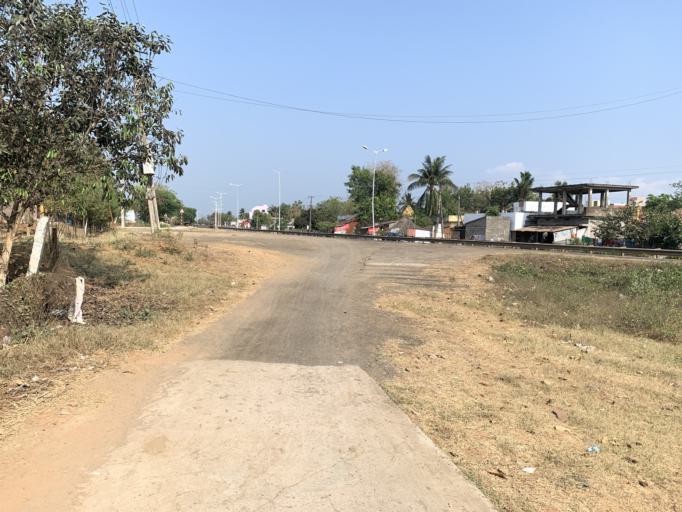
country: IN
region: Andhra Pradesh
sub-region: East Godavari
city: Peddapuram
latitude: 17.1635
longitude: 82.0256
